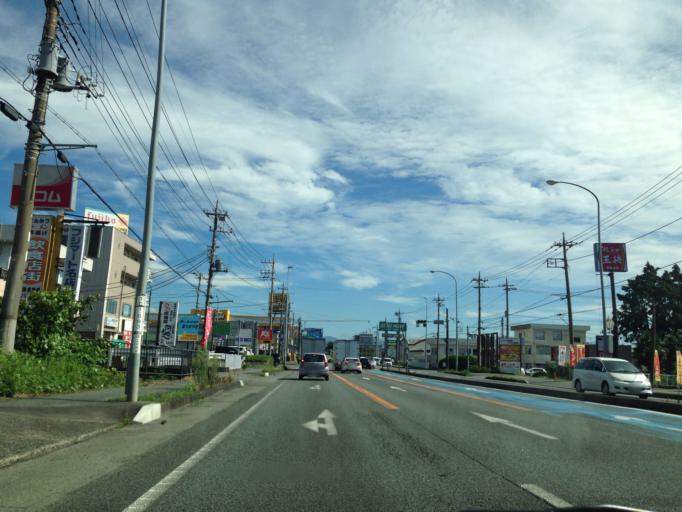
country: JP
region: Shizuoka
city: Gotemba
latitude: 35.3074
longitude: 138.9249
